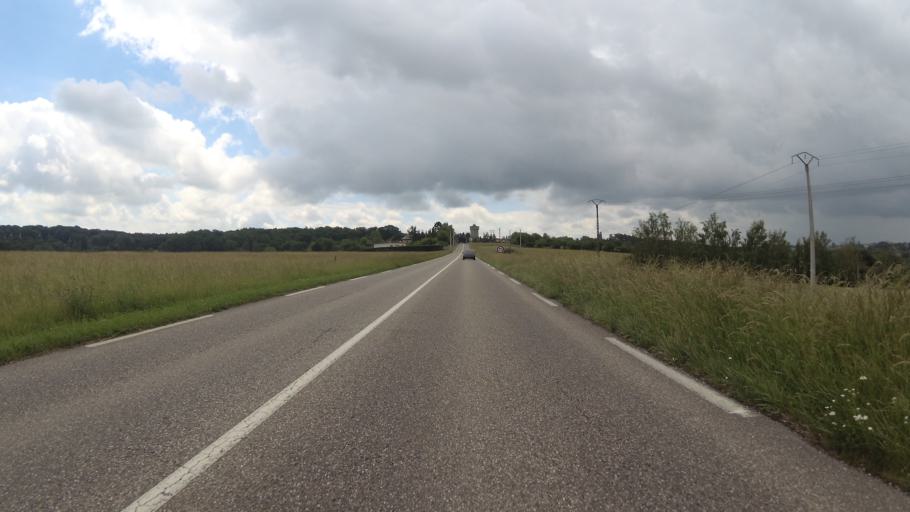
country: FR
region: Lorraine
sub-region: Departement de la Moselle
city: Remelfing
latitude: 49.0825
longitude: 7.0817
